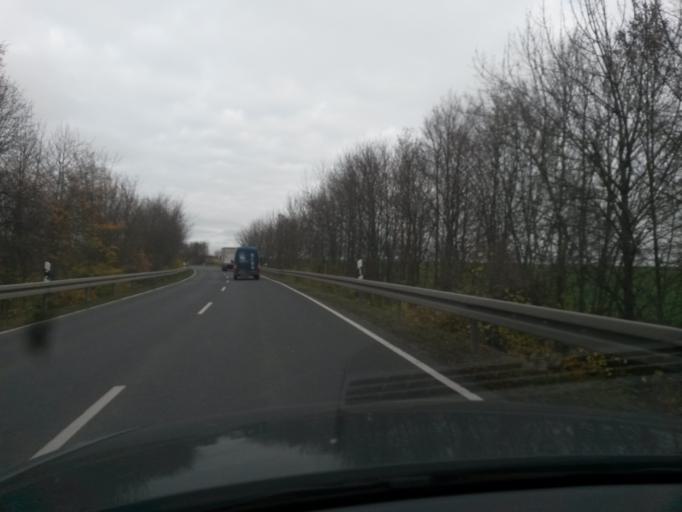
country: DE
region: Bavaria
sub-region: Regierungsbezirk Unterfranken
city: Estenfeld
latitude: 49.8335
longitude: 9.9889
